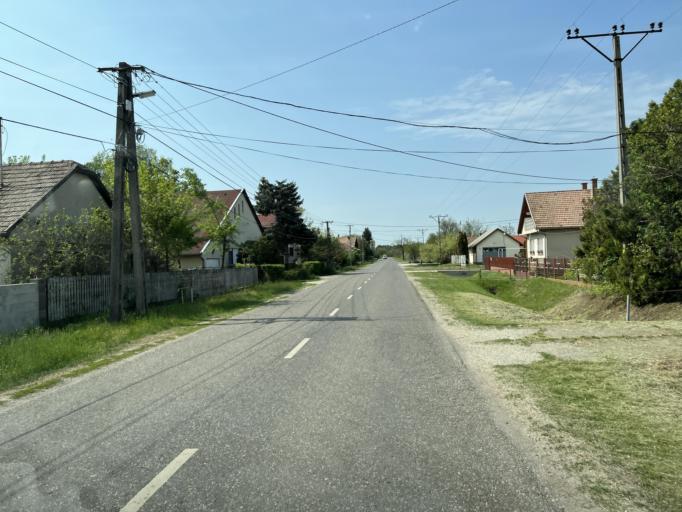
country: HU
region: Pest
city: Tortel
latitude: 47.1185
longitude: 19.9243
